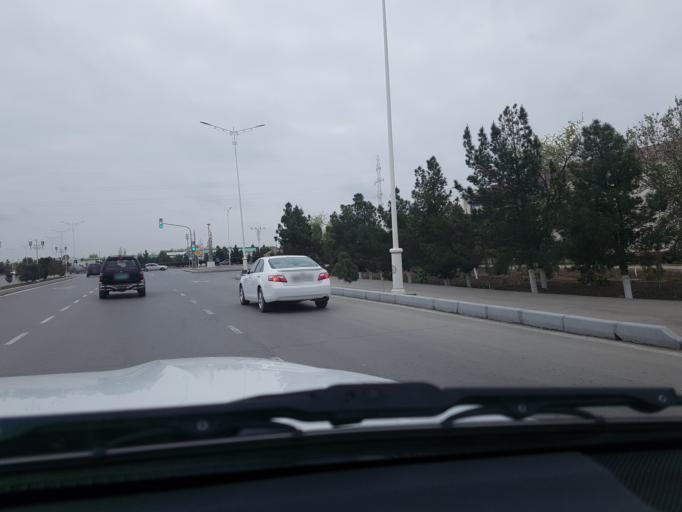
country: TM
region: Lebap
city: Turkmenabat
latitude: 39.0348
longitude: 63.5886
